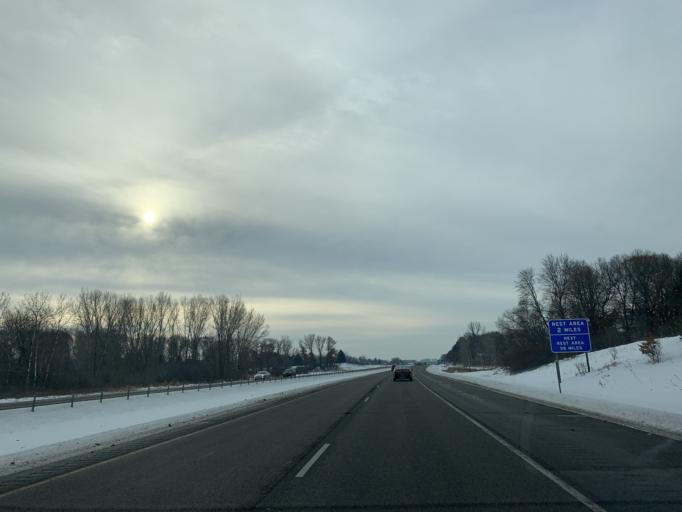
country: US
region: Minnesota
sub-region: Washington County
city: Forest Lake
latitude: 45.3023
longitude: -93.0028
